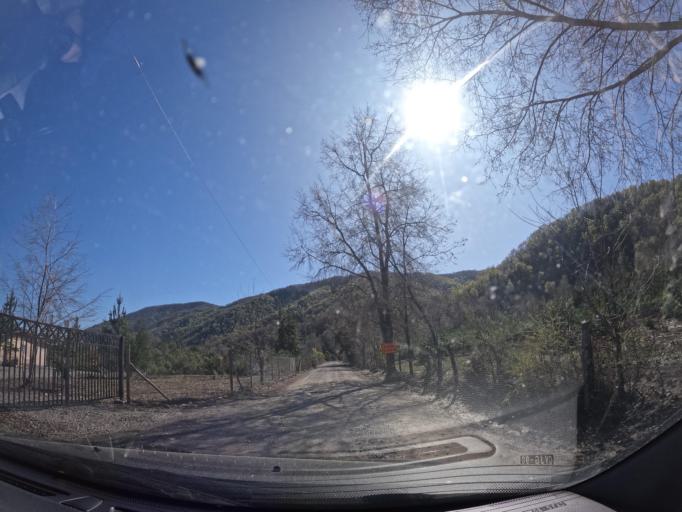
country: CL
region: Maule
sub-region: Provincia de Linares
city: Longavi
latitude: -36.2287
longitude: -71.3763
